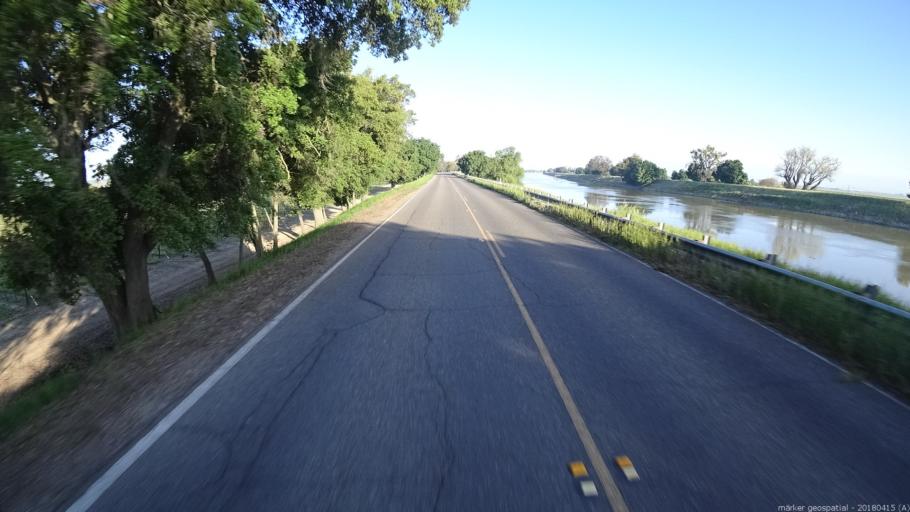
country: US
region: California
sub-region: Sacramento County
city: Walnut Grove
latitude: 38.2819
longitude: -121.5504
